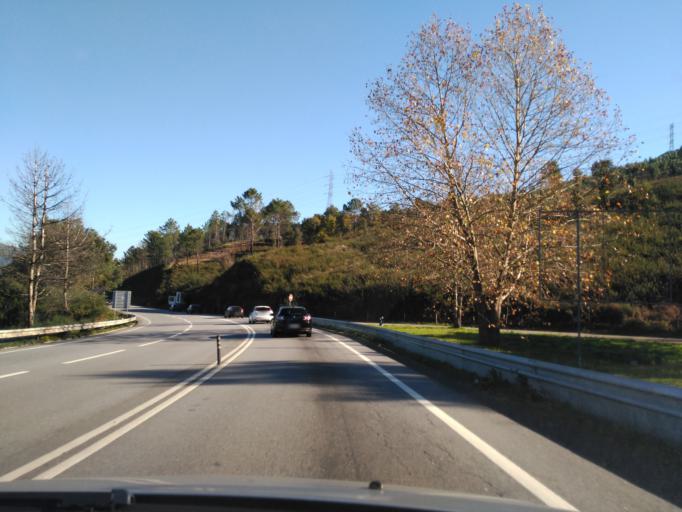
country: PT
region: Braga
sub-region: Povoa de Lanhoso
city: Povoa de Lanhoso
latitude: 41.5847
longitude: -8.3063
